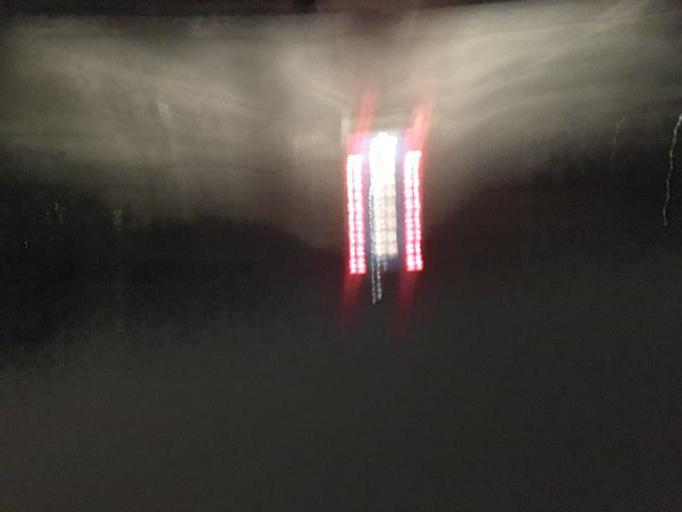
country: RU
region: Tula
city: Mendeleyevskiy
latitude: 54.1280
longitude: 37.5764
